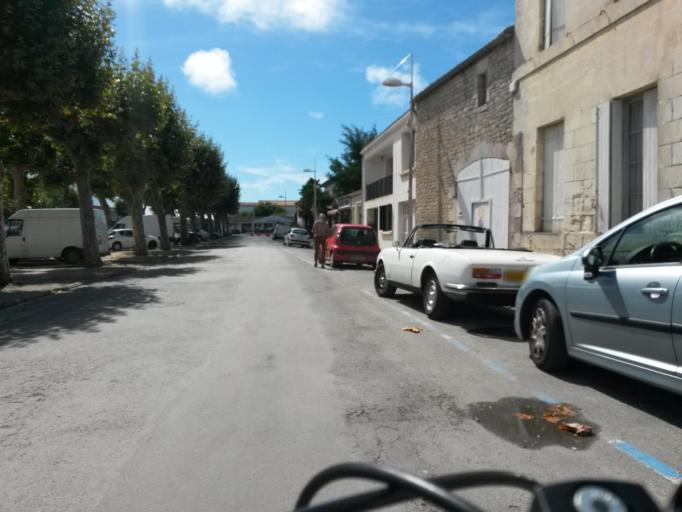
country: FR
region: Poitou-Charentes
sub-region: Departement de la Charente-Maritime
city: Dolus-d'Oleron
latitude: 45.9424
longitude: -1.3078
